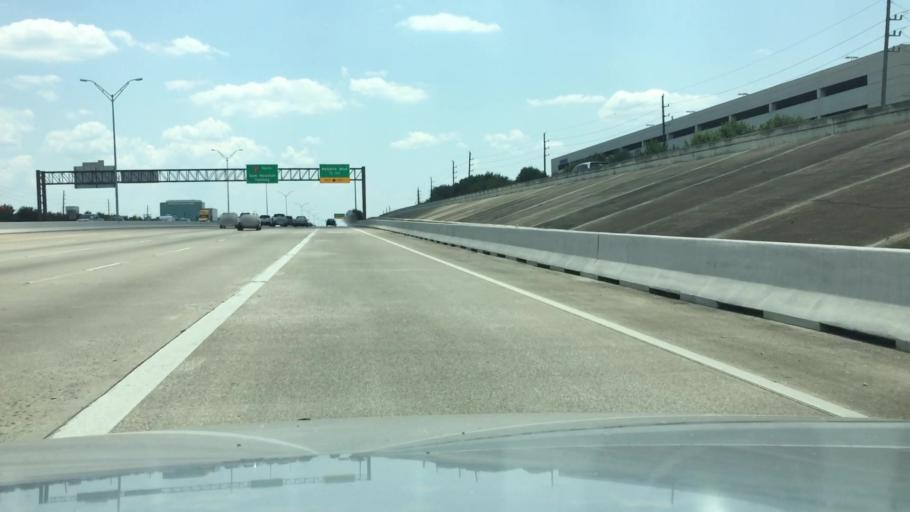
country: US
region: Texas
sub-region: Harris County
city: Bunker Hill Village
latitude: 29.7155
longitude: -95.5576
